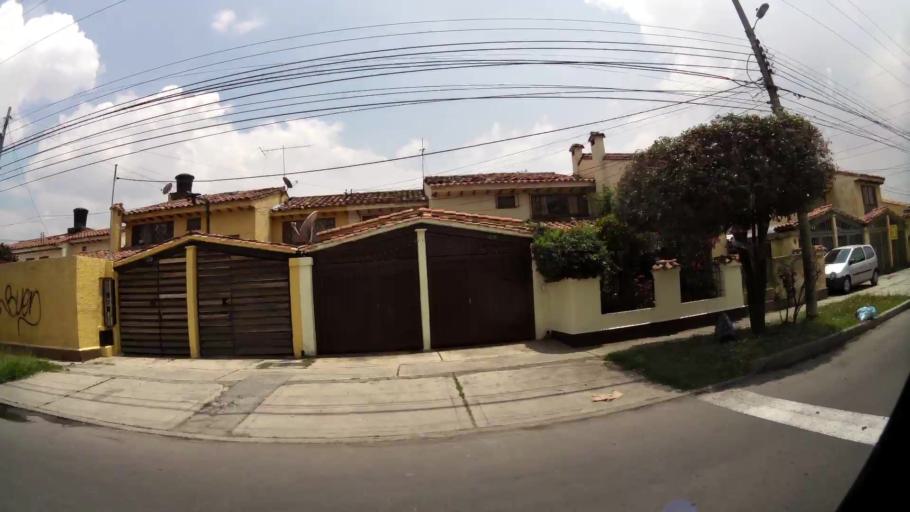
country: CO
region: Bogota D.C.
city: Barrio San Luis
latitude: 4.7396
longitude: -74.0477
